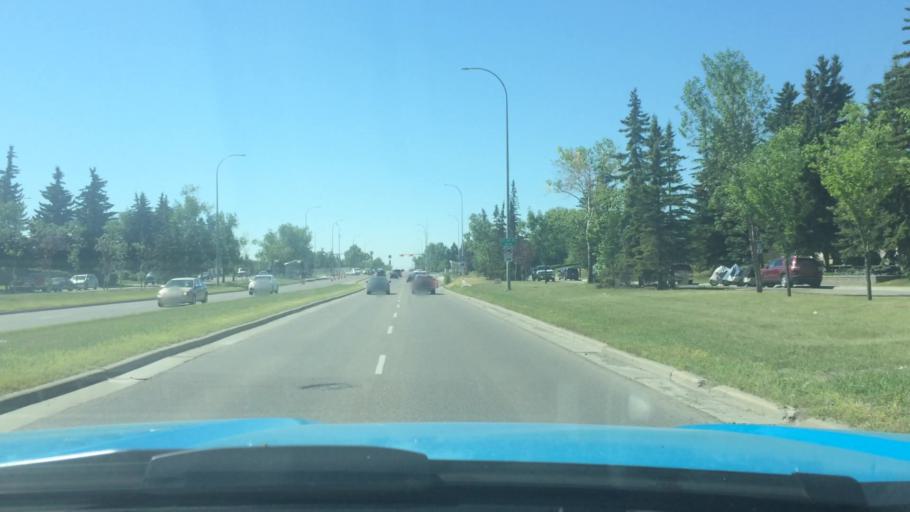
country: CA
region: Alberta
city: Calgary
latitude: 51.0838
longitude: -113.9584
